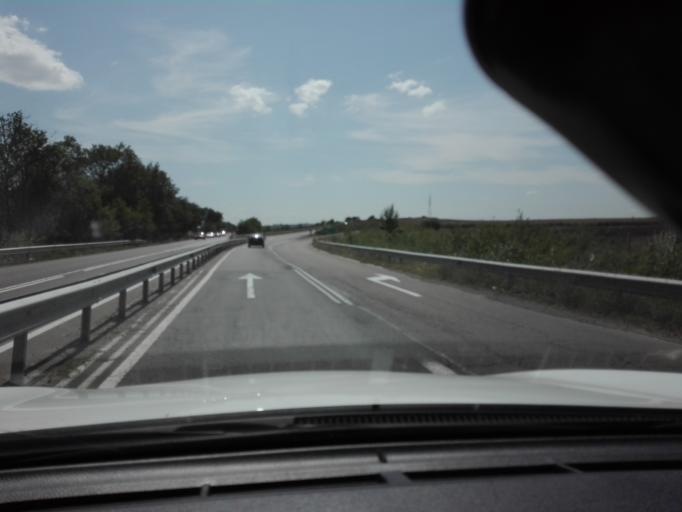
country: BG
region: Burgas
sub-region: Obshtina Kameno
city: Kameno
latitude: 42.5966
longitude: 27.3914
